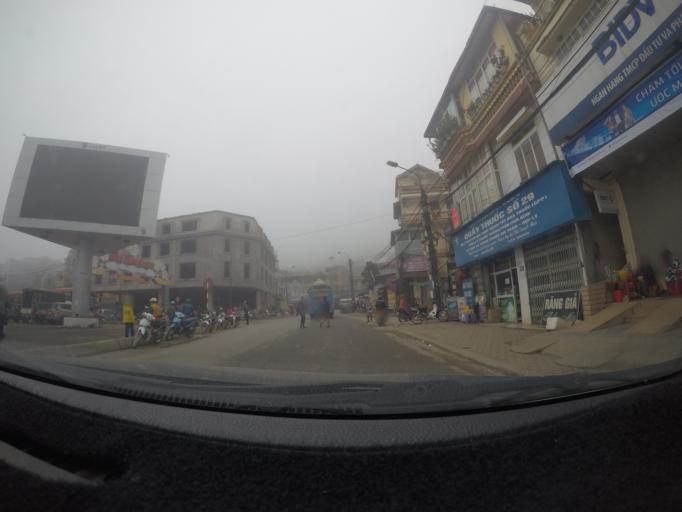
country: VN
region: Lao Cai
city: Sa Pa
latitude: 22.3384
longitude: 103.8513
